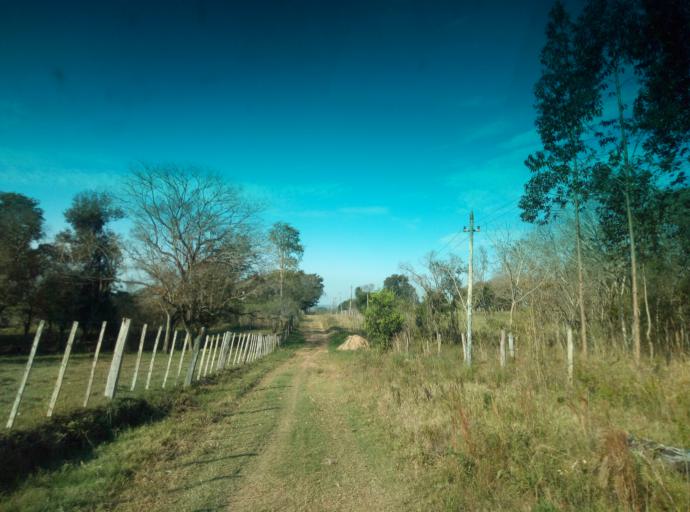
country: PY
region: Caaguazu
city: Doctor Cecilio Baez
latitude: -25.1590
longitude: -56.2303
